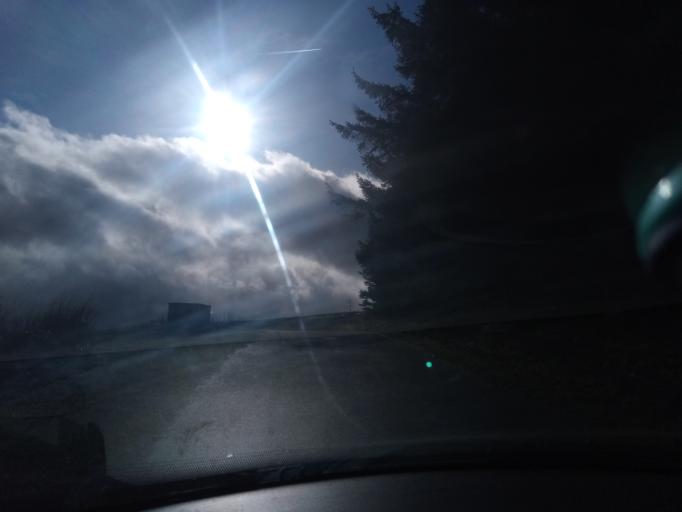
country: GB
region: England
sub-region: Northumberland
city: Rochester
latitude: 55.3278
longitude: -2.2929
